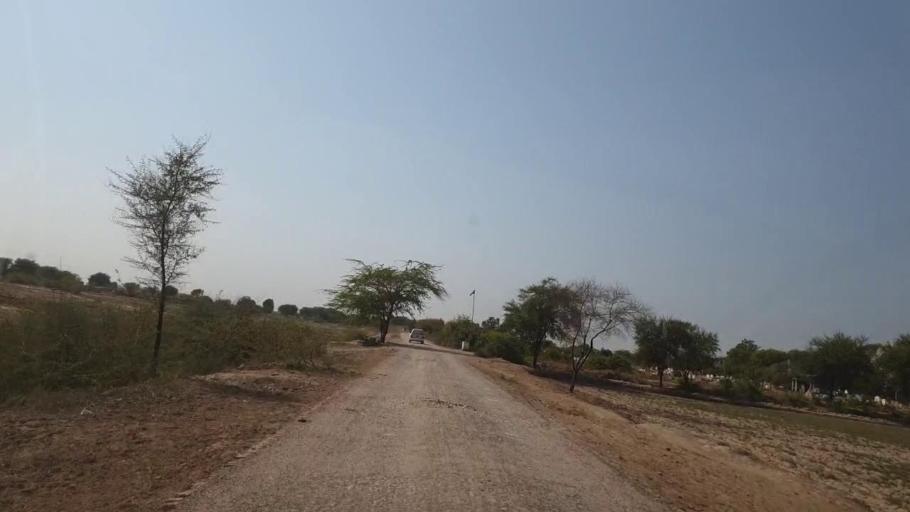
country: PK
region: Sindh
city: Nabisar
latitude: 25.0383
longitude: 69.5072
